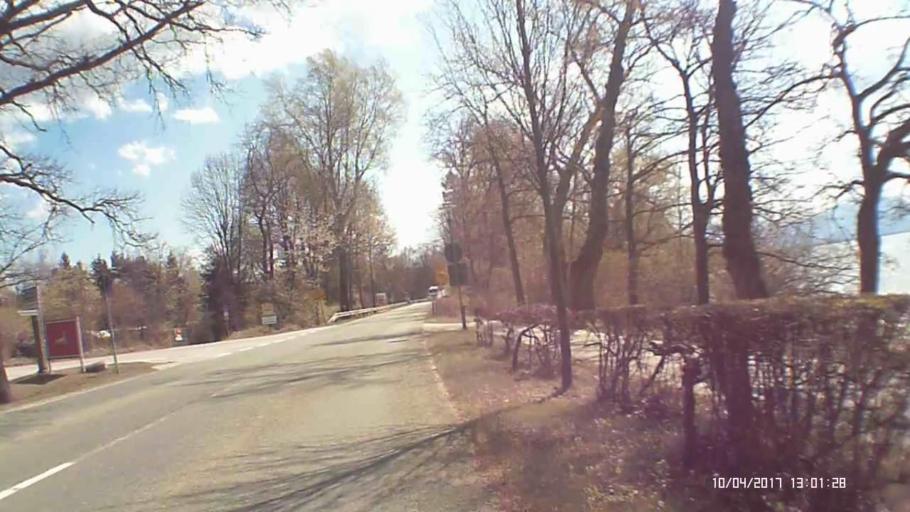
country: DE
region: Bavaria
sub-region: Upper Bavaria
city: Seeon-Seebruck
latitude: 47.9321
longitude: 12.4877
